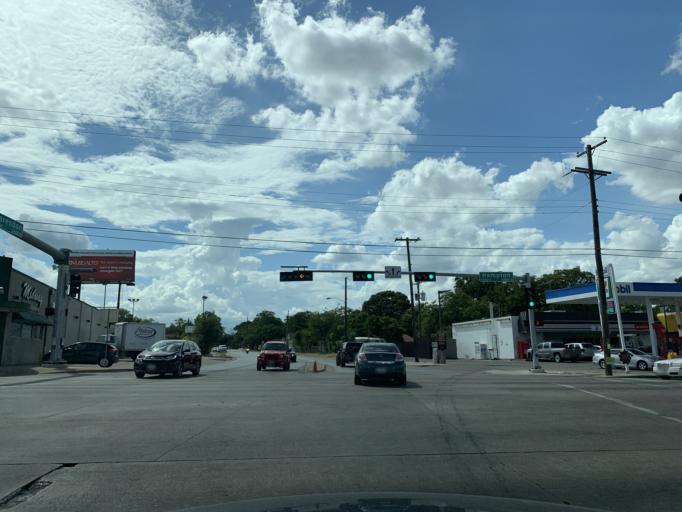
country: US
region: Texas
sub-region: Dallas County
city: Cockrell Hill
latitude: 32.7349
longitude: -96.8567
